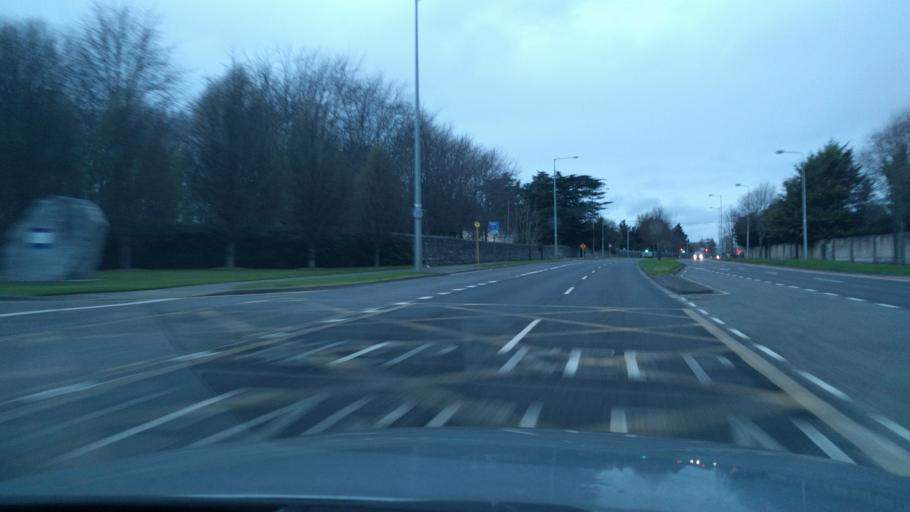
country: IE
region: Leinster
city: Clondalkin
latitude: 53.3086
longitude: -6.3864
